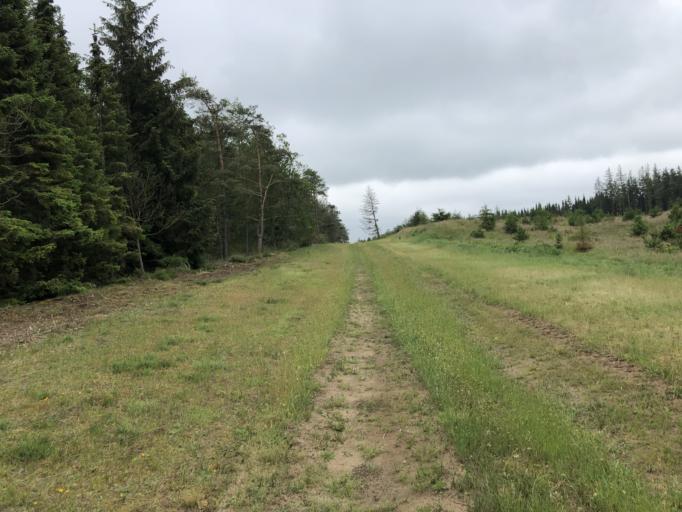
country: DK
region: Central Jutland
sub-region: Holstebro Kommune
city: Ulfborg
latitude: 56.2532
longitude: 8.3573
